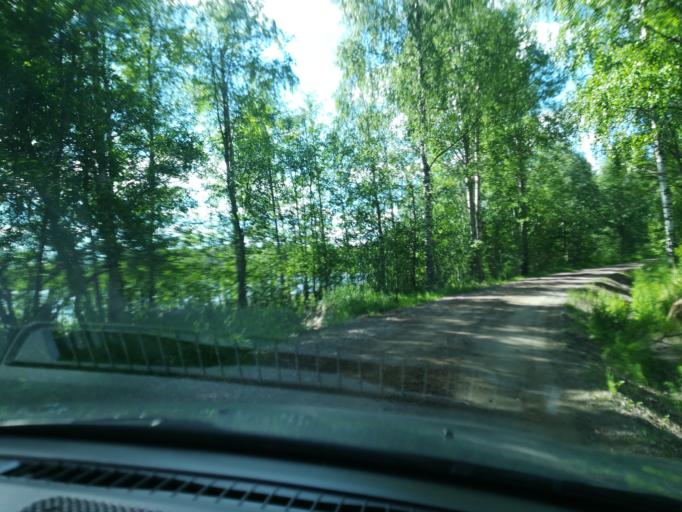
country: FI
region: Southern Savonia
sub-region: Mikkeli
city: Puumala
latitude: 61.6602
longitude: 28.1532
